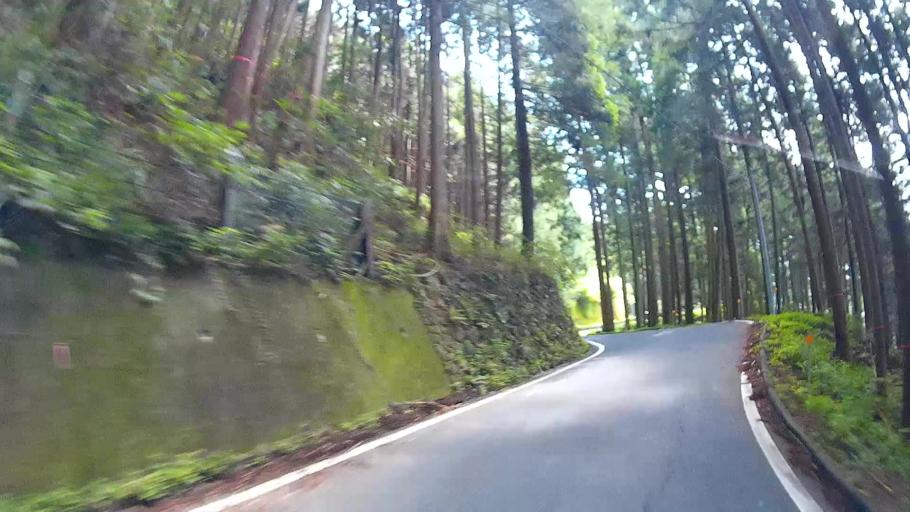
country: JP
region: Saitama
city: Chichibu
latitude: 35.9280
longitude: 139.1489
